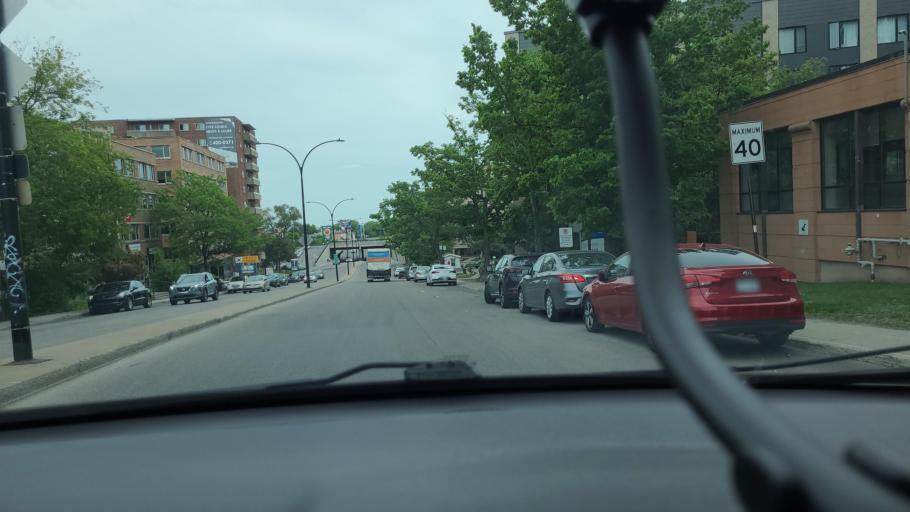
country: CA
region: Quebec
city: Saint-Raymond
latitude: 45.4635
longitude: -73.6285
